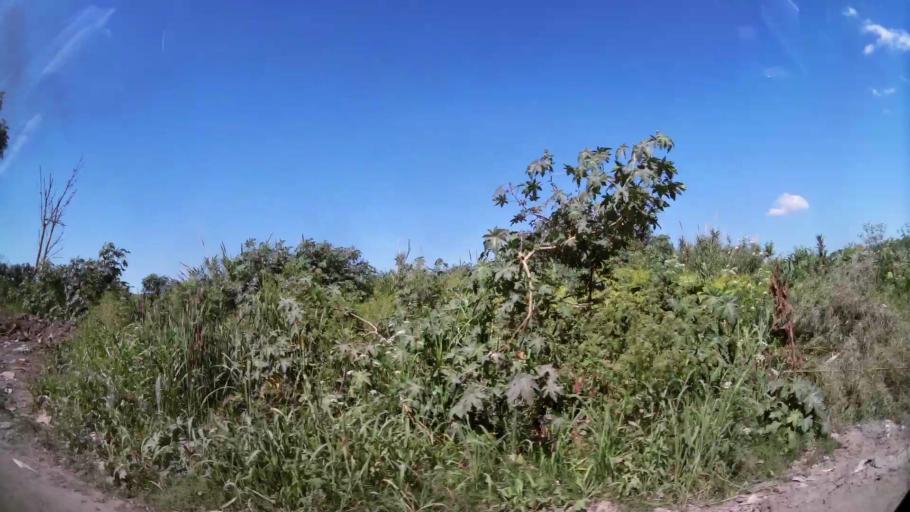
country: AR
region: Buenos Aires F.D.
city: Villa Lugano
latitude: -34.7016
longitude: -58.4703
